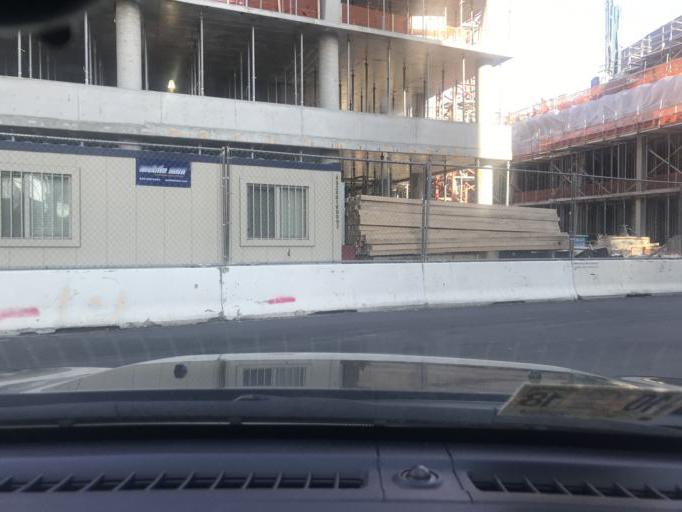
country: US
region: Virginia
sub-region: Arlington County
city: Arlington
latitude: 38.8946
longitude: -77.0767
